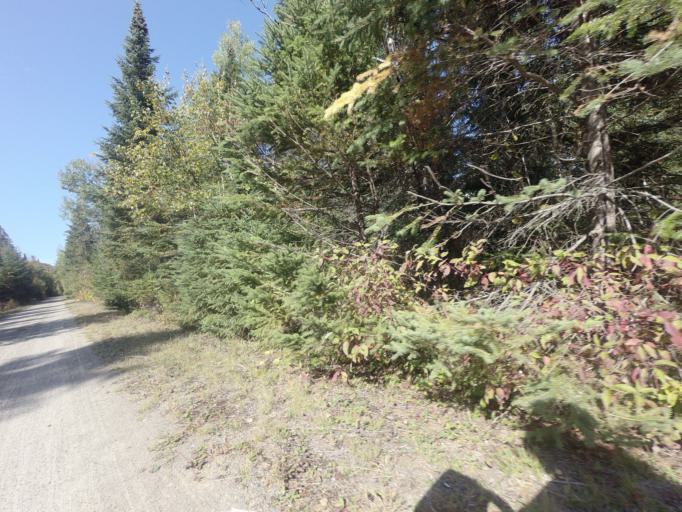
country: CA
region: Quebec
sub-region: Laurentides
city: Sainte-Agathe-des-Monts
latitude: 46.0796
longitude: -74.3246
